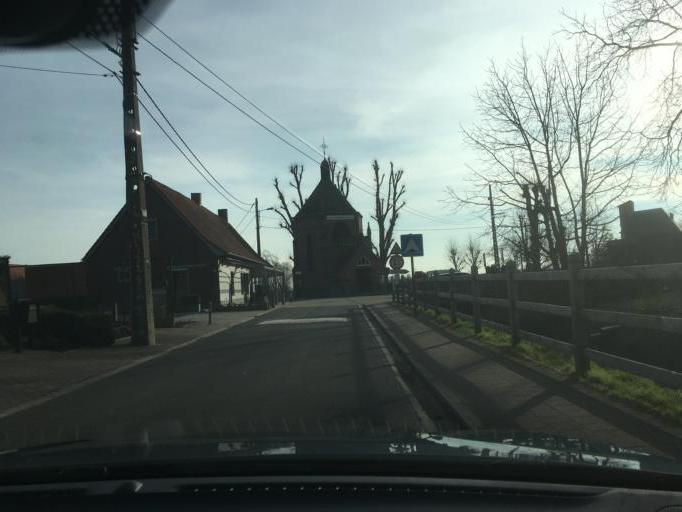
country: BE
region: Flanders
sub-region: Provincie West-Vlaanderen
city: Meulebeke
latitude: 50.9420
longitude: 3.2820
